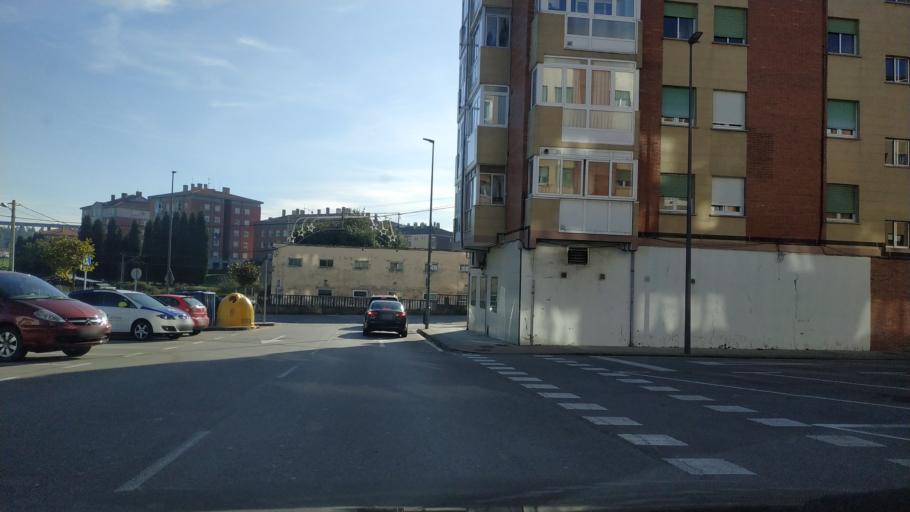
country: ES
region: Asturias
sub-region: Province of Asturias
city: Corvera de Asturias
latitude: 43.5388
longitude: -5.8886
